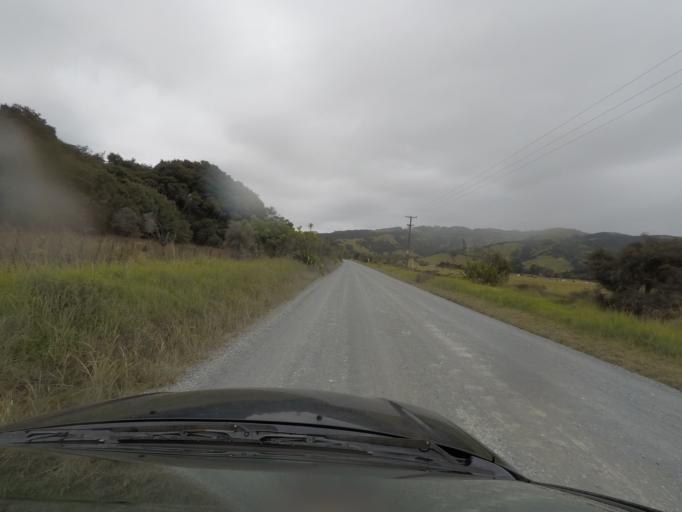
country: NZ
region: Auckland
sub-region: Auckland
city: Warkworth
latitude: -36.2543
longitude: 174.7187
